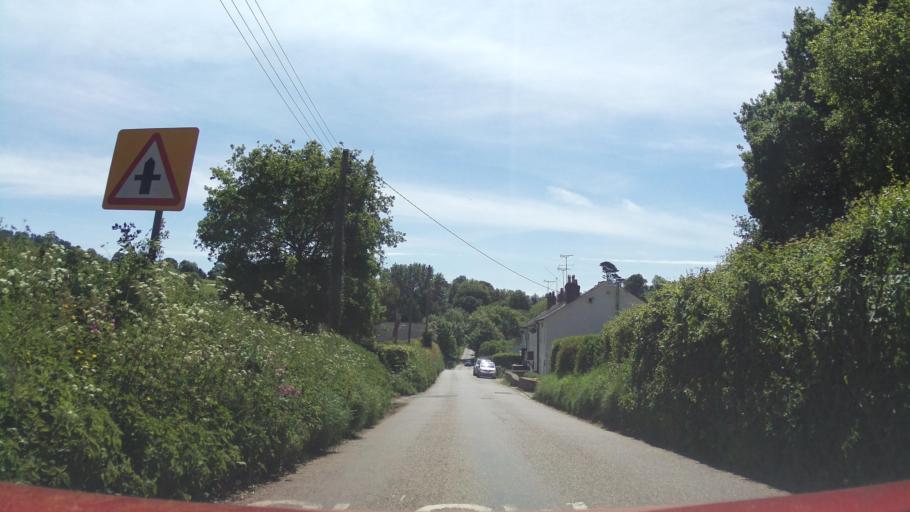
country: GB
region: England
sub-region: Devon
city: Newton Poppleford
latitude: 50.7210
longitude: -3.2835
